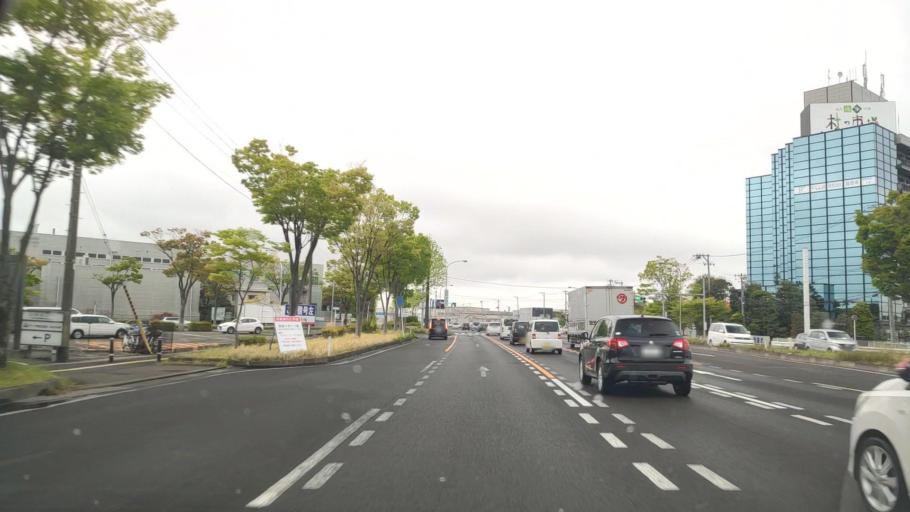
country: JP
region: Miyagi
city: Sendai-shi
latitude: 38.2560
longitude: 140.9348
